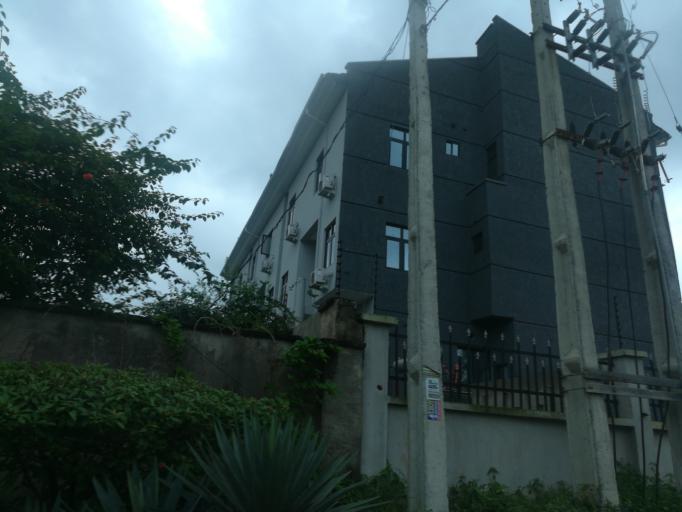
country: NG
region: Lagos
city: Ikeja
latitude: 6.6166
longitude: 3.3484
